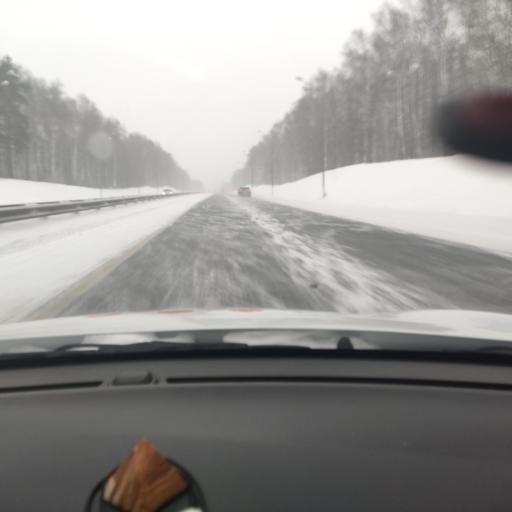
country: RU
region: Tatarstan
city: Osinovo
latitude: 55.8315
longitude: 48.8496
